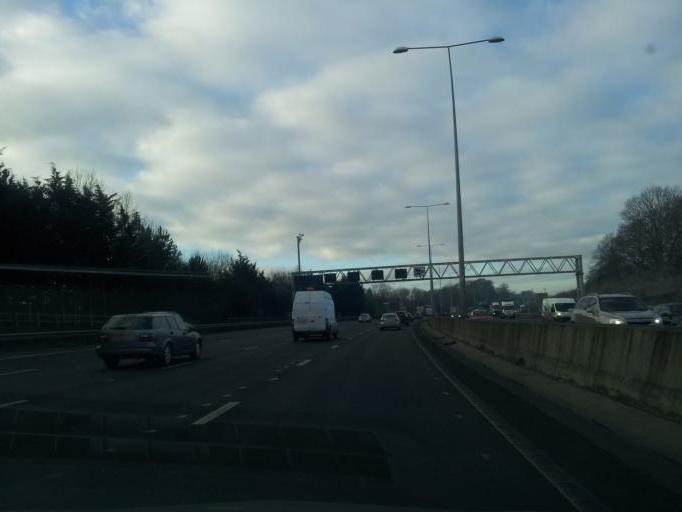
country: GB
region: England
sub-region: Hertfordshire
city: Chorleywood
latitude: 51.6746
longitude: -0.4634
